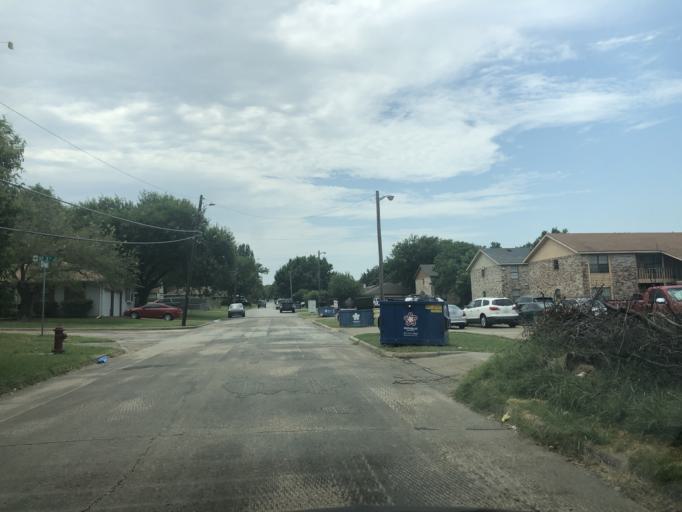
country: US
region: Texas
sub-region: Dallas County
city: Grand Prairie
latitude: 32.7352
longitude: -97.0010
